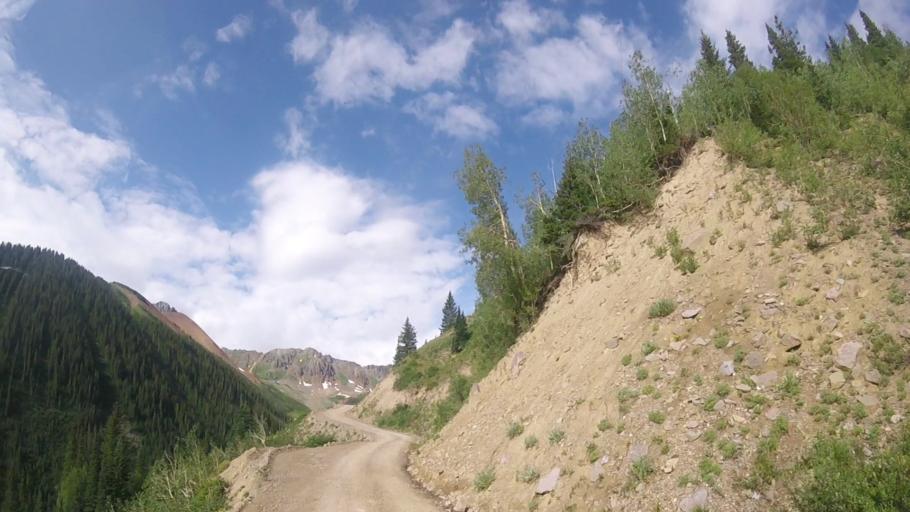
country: US
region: Colorado
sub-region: San Juan County
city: Silverton
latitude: 37.8470
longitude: -107.7600
